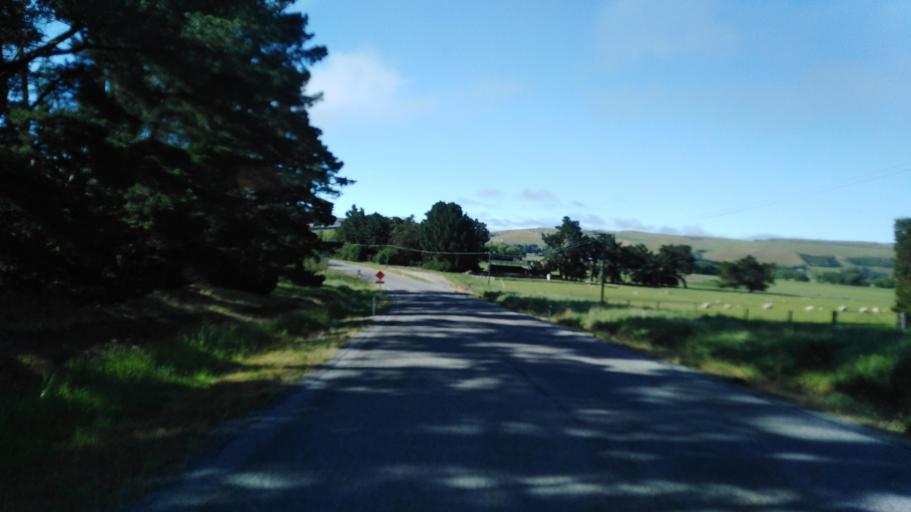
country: NZ
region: Canterbury
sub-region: Hurunui District
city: Amberley
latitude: -42.9497
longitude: 172.7076
